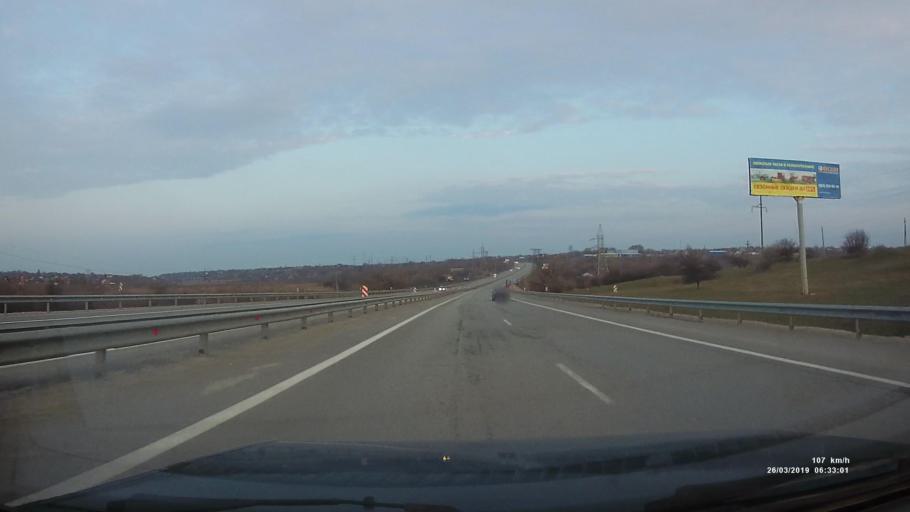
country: RU
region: Rostov
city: Chaltyr
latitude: 47.2711
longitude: 39.4994
